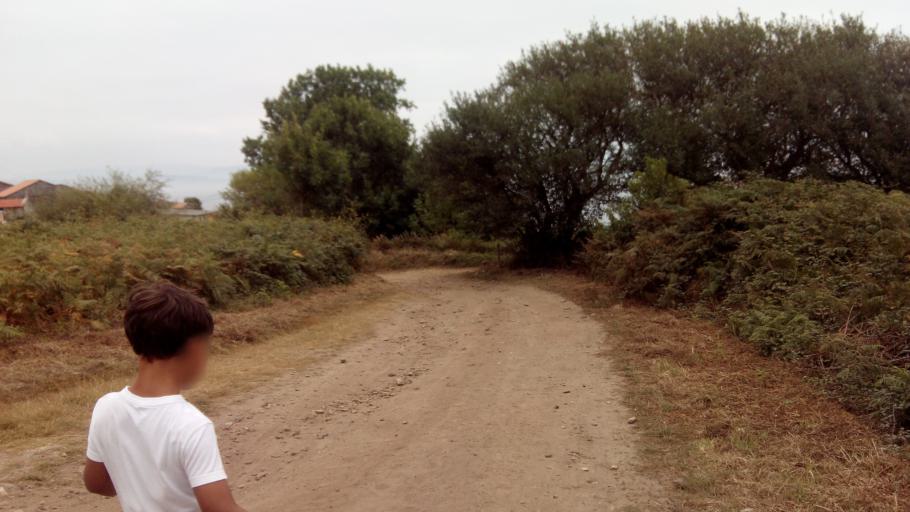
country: ES
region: Galicia
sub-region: Provincia de Pontevedra
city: Sanxenxo
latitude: 42.3739
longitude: -8.9358
